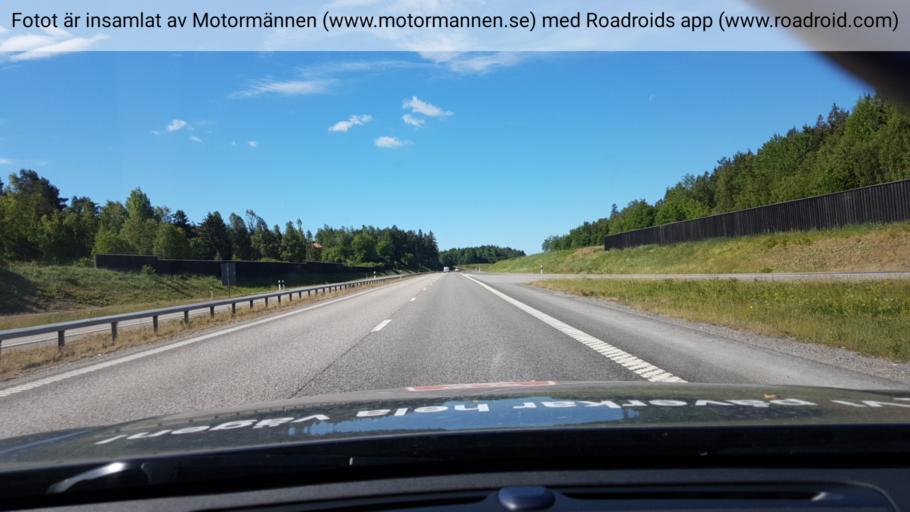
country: SE
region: Stockholm
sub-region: Nynashamns Kommun
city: Osmo
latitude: 58.9933
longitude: 17.9301
